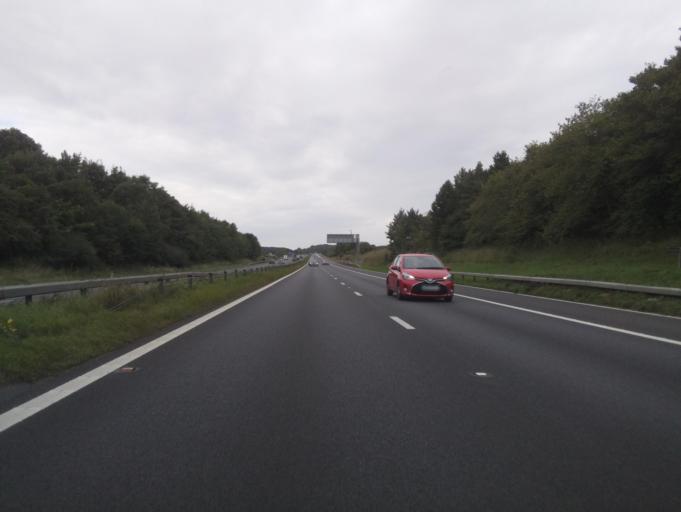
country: GB
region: England
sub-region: County Durham
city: Bishop Middleham
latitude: 54.6706
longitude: -1.4996
